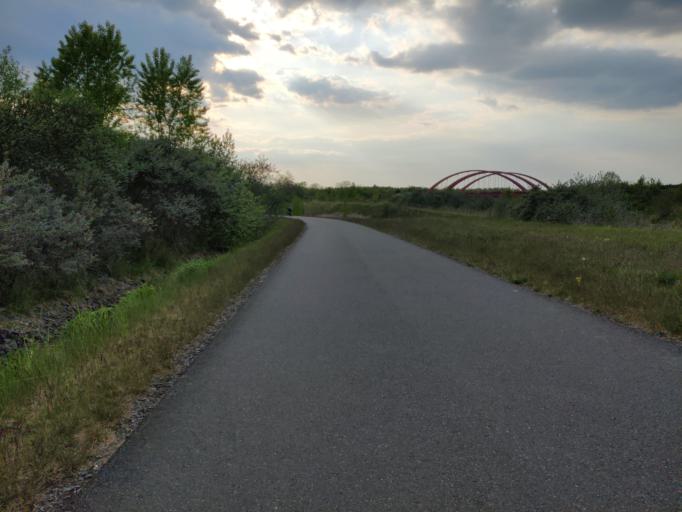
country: DE
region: Saxony
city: Rotha
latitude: 51.2477
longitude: 12.4274
